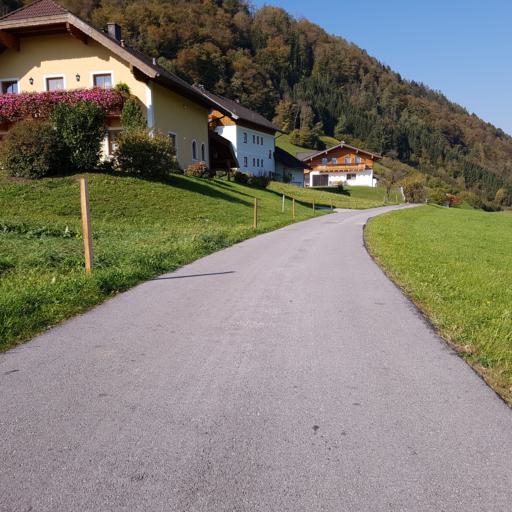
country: AT
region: Salzburg
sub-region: Politischer Bezirk Hallein
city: Hallein
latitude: 47.6642
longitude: 13.1131
